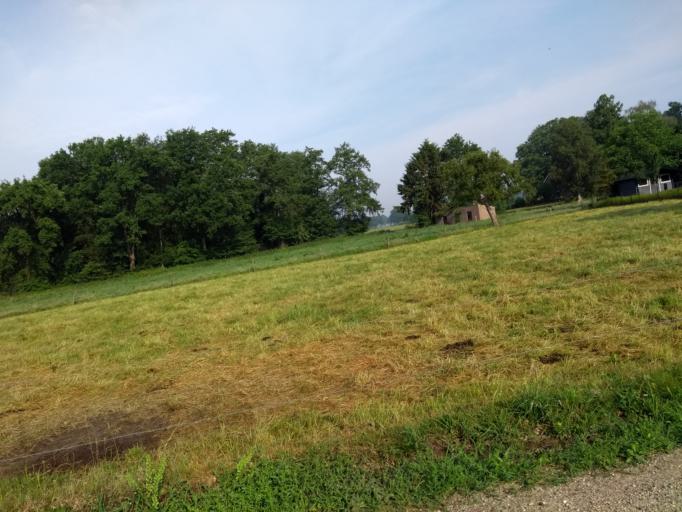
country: NL
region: Overijssel
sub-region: Gemeente Almelo
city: Almelo
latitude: 52.3864
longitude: 6.7072
